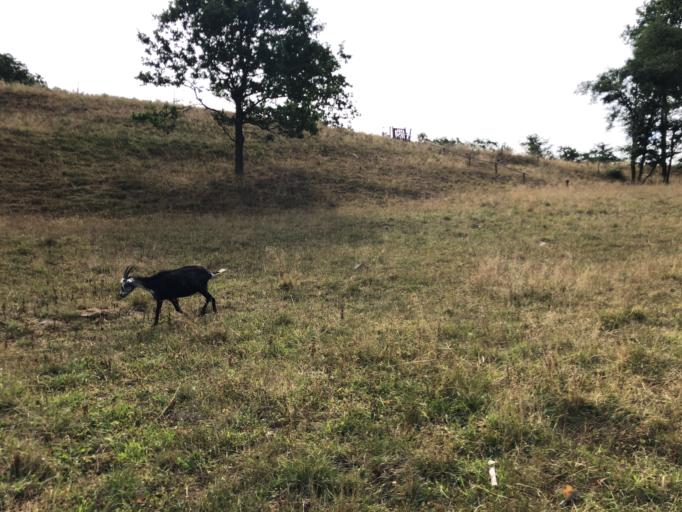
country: DK
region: South Denmark
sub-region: Vejle Kommune
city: Egtved
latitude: 55.6522
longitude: 9.2856
